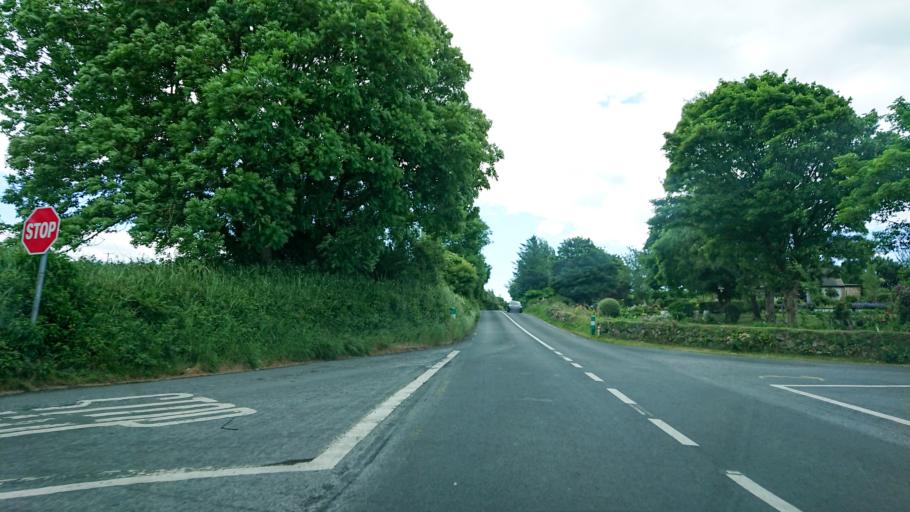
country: IE
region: Munster
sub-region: Waterford
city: Tra Mhor
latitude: 52.1829
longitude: -7.1733
